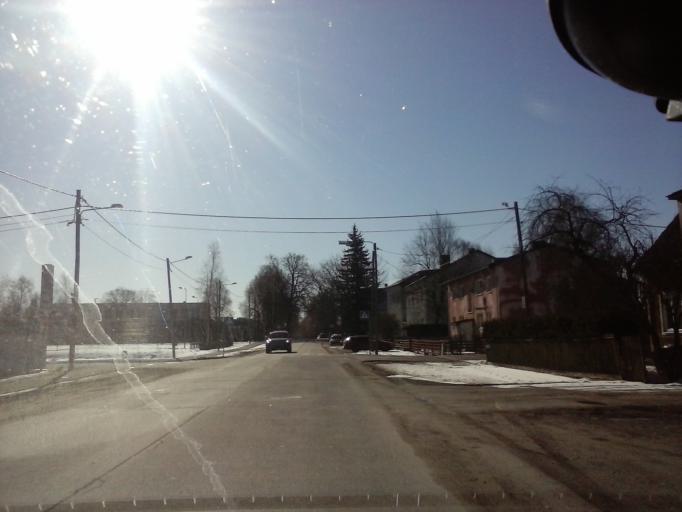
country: EE
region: Tartu
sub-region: Tartu linn
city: Tartu
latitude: 58.3633
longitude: 26.7033
